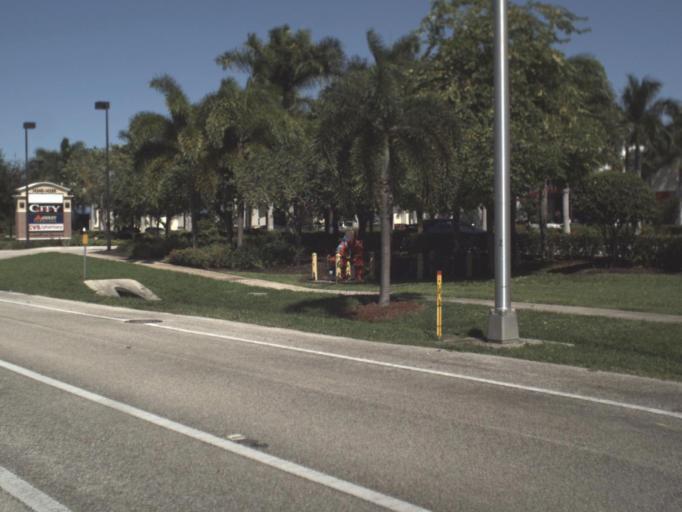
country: US
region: Florida
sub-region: Collier County
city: Naples Park
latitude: 26.2991
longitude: -81.8026
